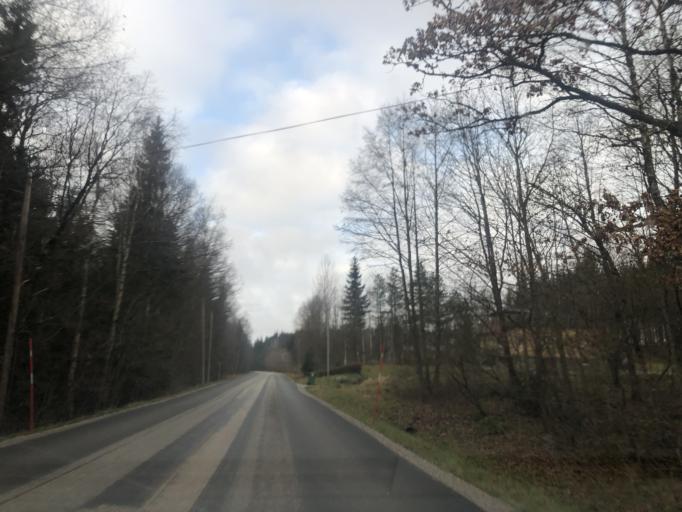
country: SE
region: Vaestra Goetaland
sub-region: Tranemo Kommun
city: Langhem
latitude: 57.7035
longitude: 13.2971
